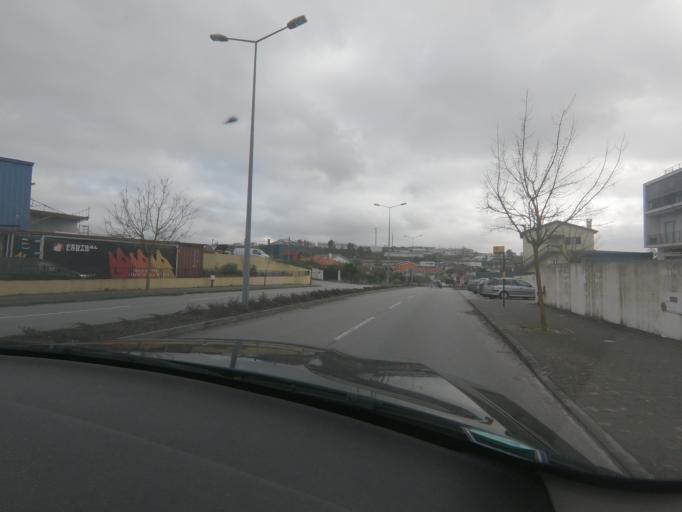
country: PT
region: Viseu
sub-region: Viseu
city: Abraveses
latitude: 40.6851
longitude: -7.9274
